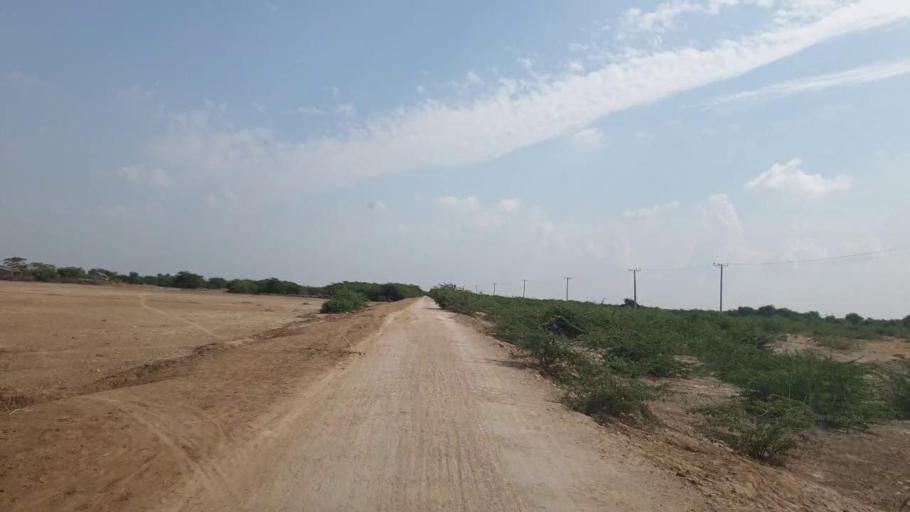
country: PK
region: Sindh
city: Badin
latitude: 24.4781
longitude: 68.6178
